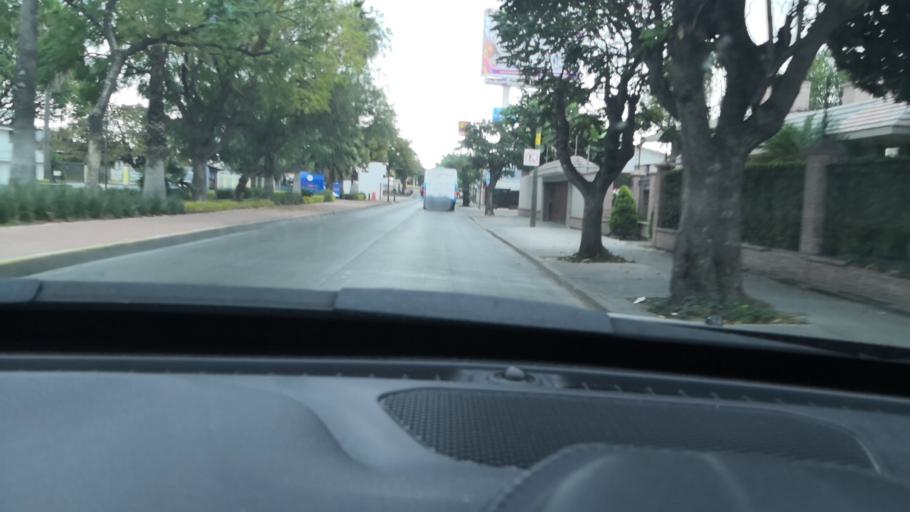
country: MX
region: Guanajuato
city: Leon
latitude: 21.1086
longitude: -101.6646
